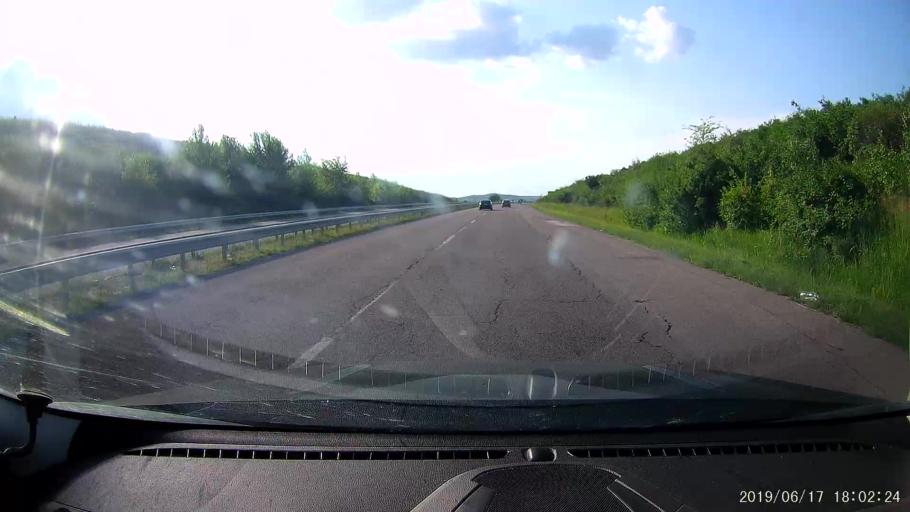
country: BG
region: Khaskovo
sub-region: Obshtina Svilengrad
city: Svilengrad
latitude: 41.7591
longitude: 26.2313
